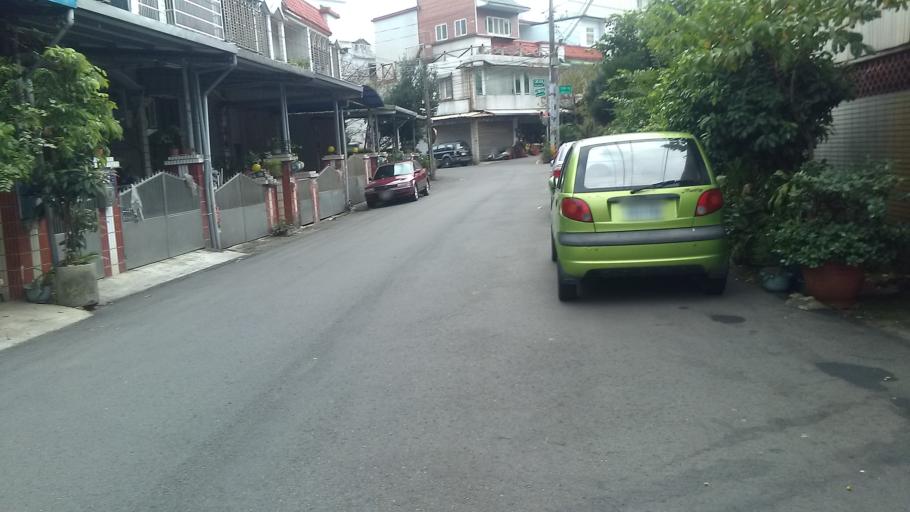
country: TW
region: Taiwan
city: Taoyuan City
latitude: 24.9523
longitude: 121.2627
